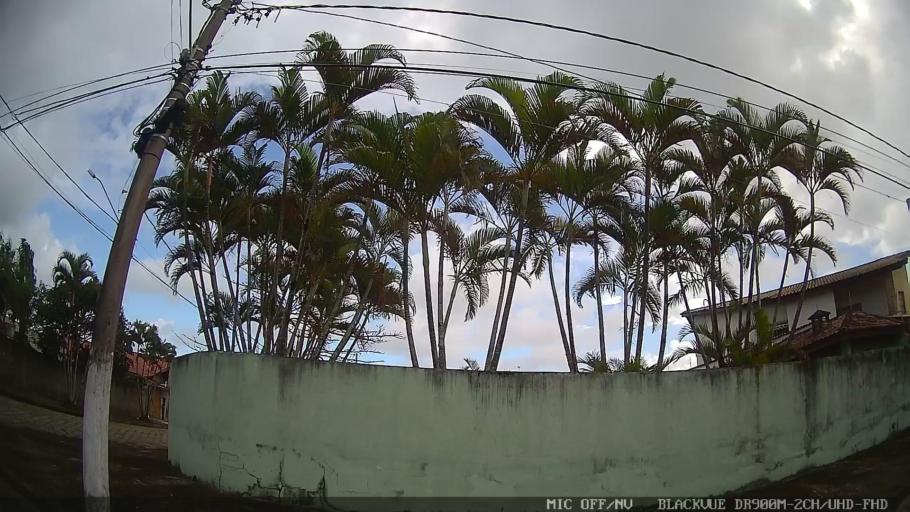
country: BR
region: Sao Paulo
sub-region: Itanhaem
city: Itanhaem
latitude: -24.2187
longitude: -46.8501
